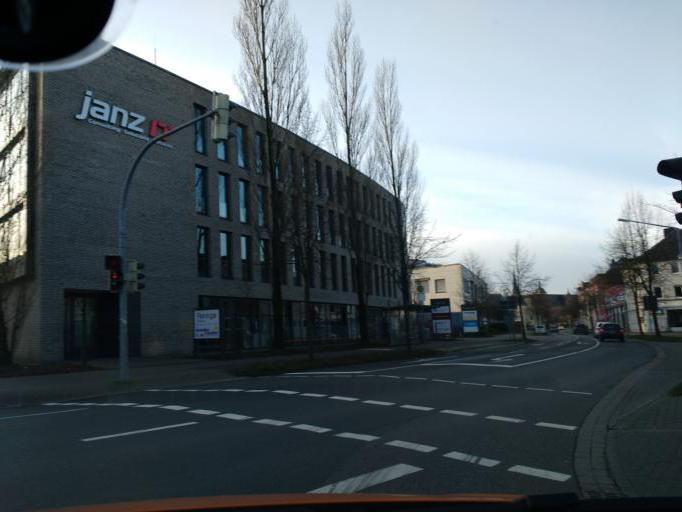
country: DE
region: Lower Saxony
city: Oldenburg
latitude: 53.1416
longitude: 8.2240
